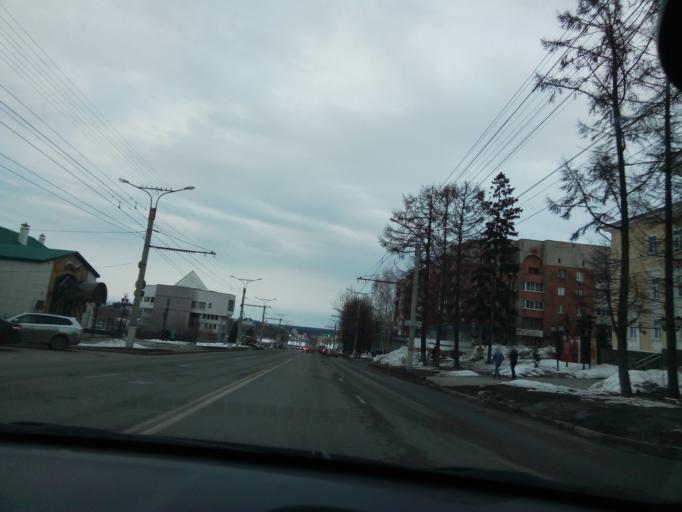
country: RU
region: Chuvashia
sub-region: Cheboksarskiy Rayon
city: Cheboksary
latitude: 56.1407
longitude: 47.2445
